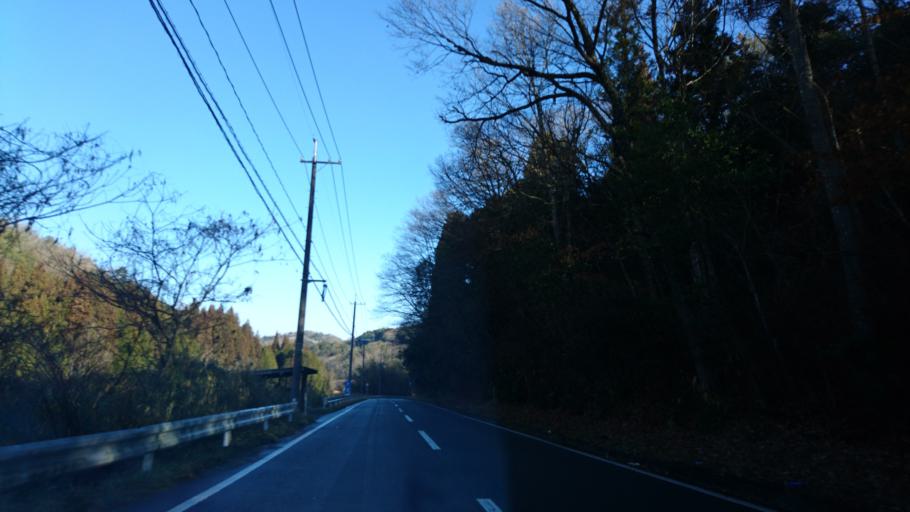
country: JP
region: Okayama
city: Takahashi
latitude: 34.8153
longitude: 133.6748
